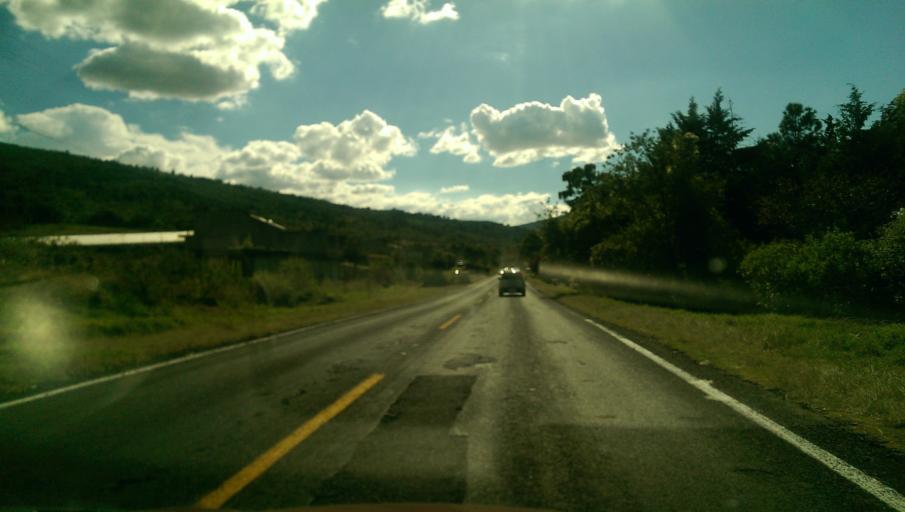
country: MX
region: Michoacan
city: Tzintzuntzan
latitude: 19.6377
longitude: -101.5507
